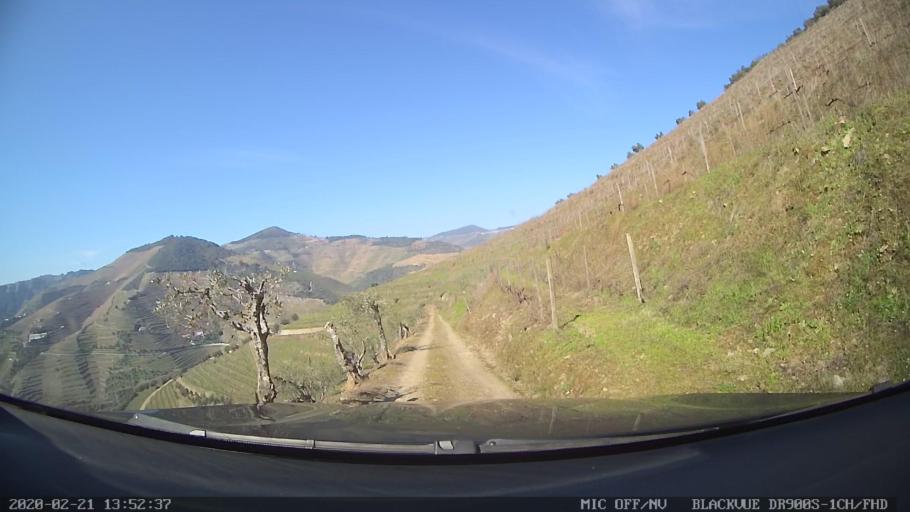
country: PT
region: Viseu
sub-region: Tabuaco
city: Tabuaco
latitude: 41.1755
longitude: -7.5444
